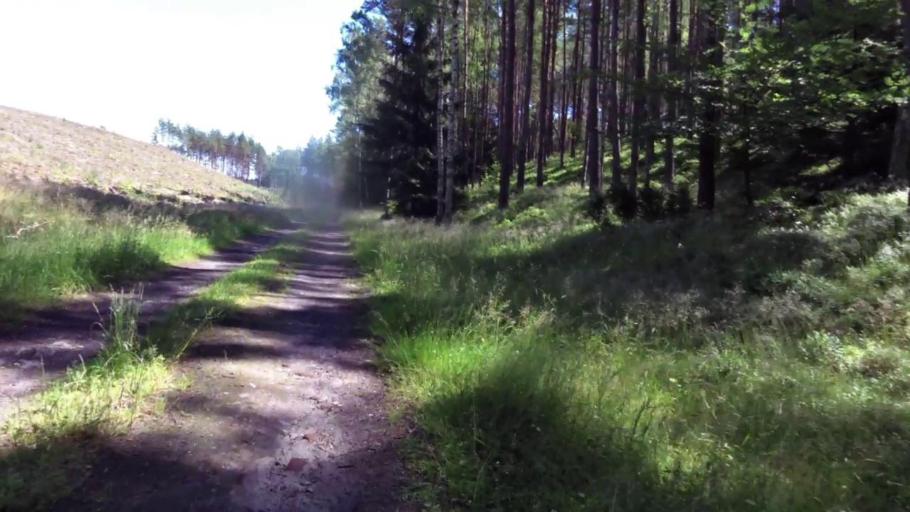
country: PL
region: West Pomeranian Voivodeship
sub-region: Powiat swidwinski
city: Polczyn-Zdroj
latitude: 53.9052
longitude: 16.1057
